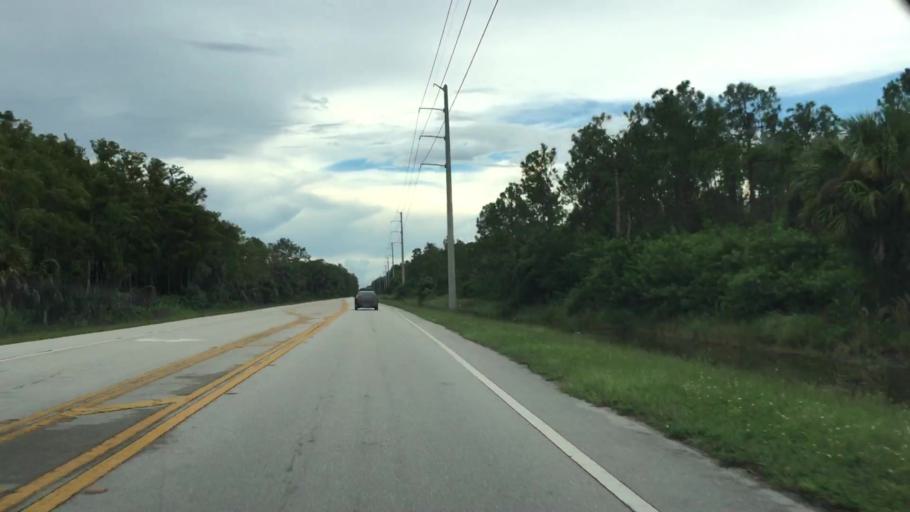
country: US
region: Florida
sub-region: Collier County
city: Orangetree
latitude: 26.3284
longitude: -81.5950
